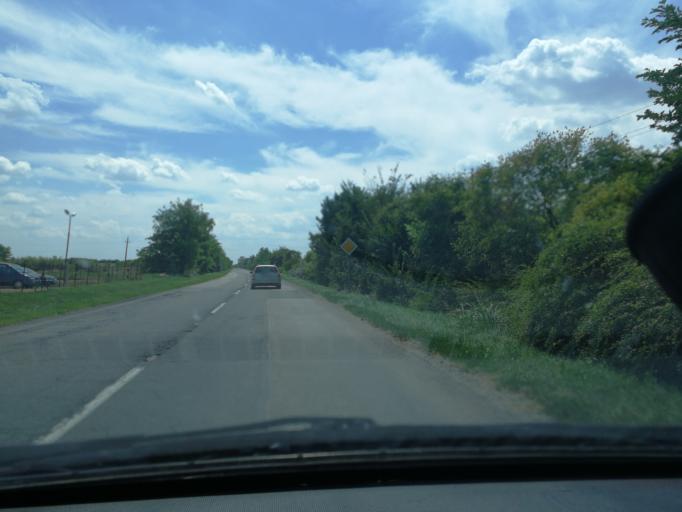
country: HU
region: Bacs-Kiskun
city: Tass
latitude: 47.0170
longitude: 19.0182
